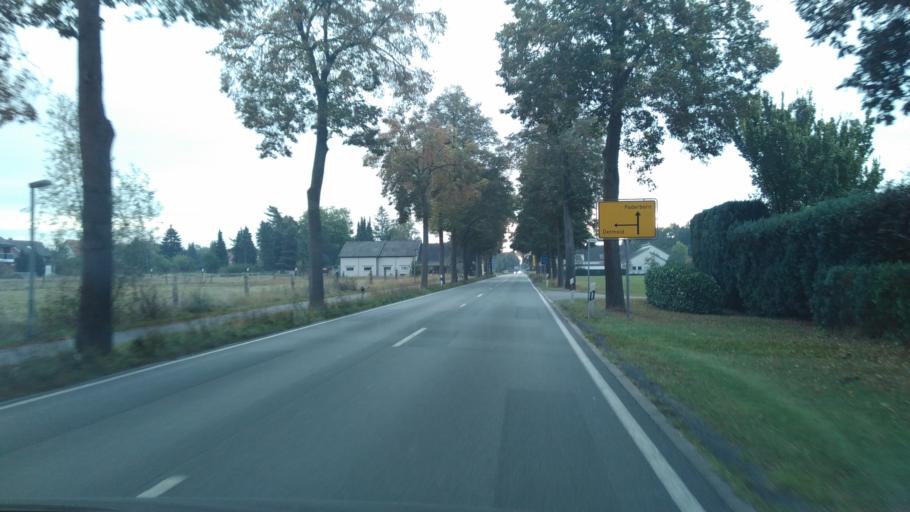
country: DE
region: North Rhine-Westphalia
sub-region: Regierungsbezirk Detmold
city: Verl
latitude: 51.8759
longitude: 8.5306
